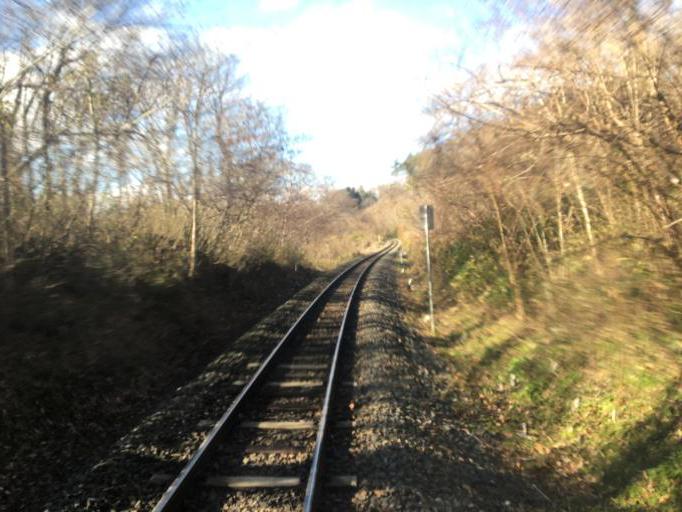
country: JP
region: Iwate
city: Ichinoseki
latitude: 38.9937
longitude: 141.2885
